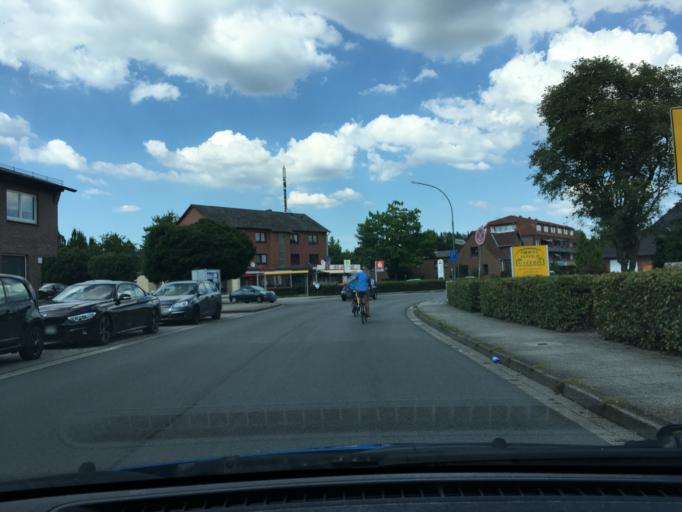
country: DE
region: Lower Saxony
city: Harmstorf
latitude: 53.3943
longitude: 10.0377
